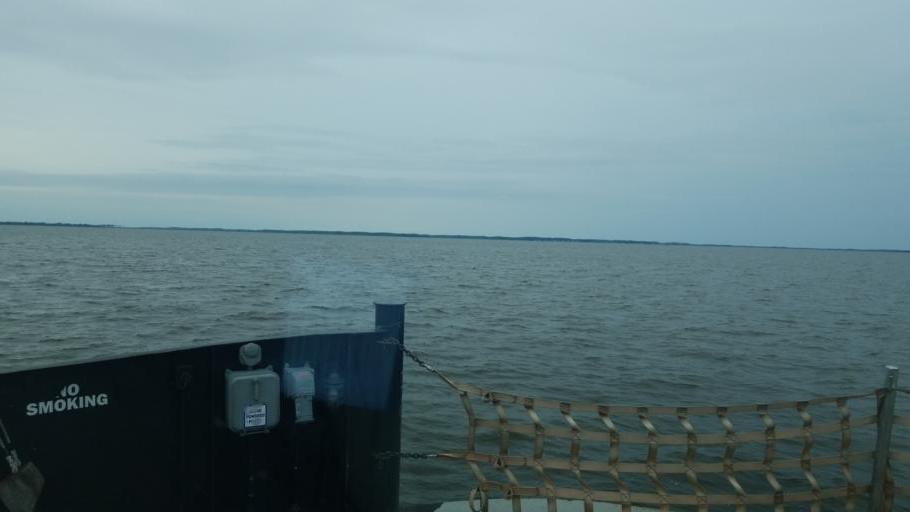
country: US
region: North Carolina
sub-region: Currituck County
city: Currituck
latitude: 36.4565
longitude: -75.9862
